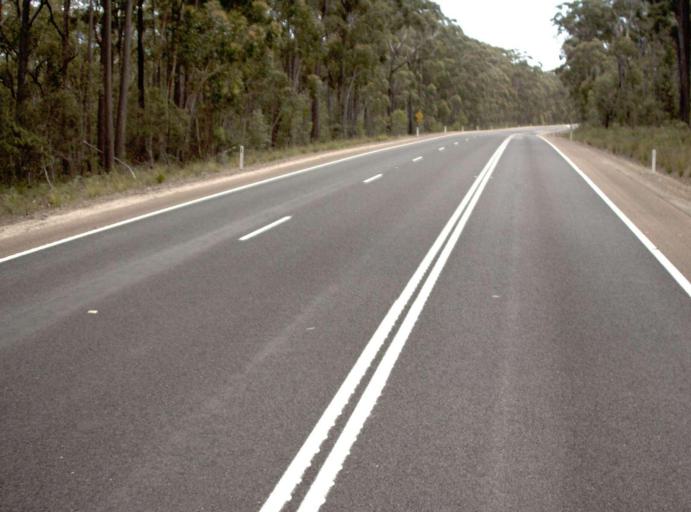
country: AU
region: New South Wales
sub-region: Bega Valley
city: Eden
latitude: -37.5049
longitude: 149.5329
